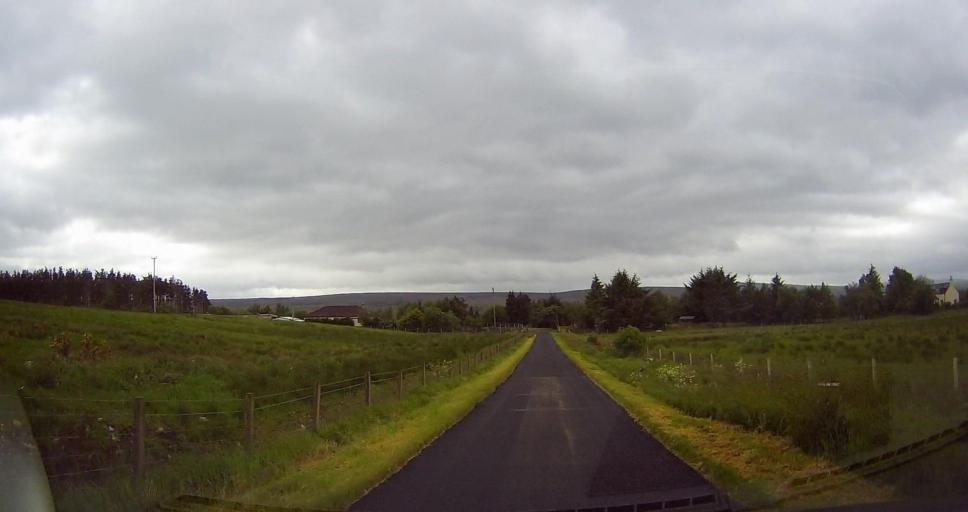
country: GB
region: Scotland
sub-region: Highland
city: Evanton
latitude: 58.0765
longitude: -4.4623
